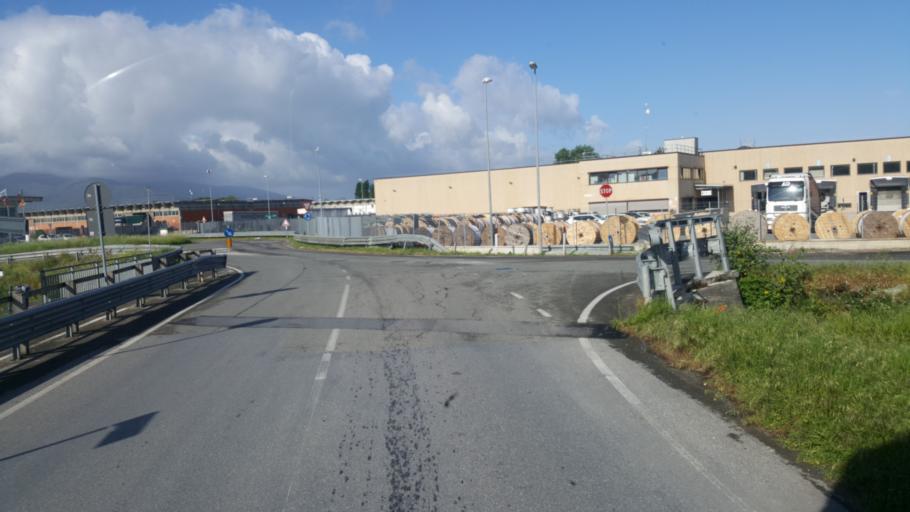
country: IT
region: Tuscany
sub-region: Provincia di Lucca
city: Porcari
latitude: 43.8504
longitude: 10.6009
